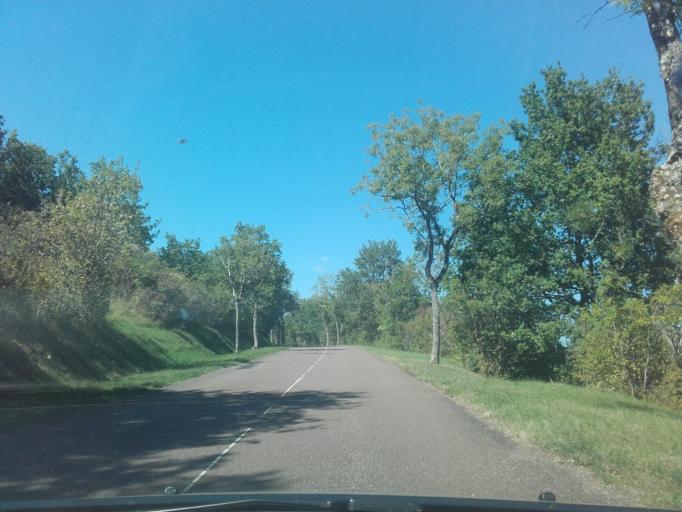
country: FR
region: Bourgogne
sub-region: Departement de la Cote-d'Or
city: Nolay
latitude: 46.9461
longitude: 4.6857
